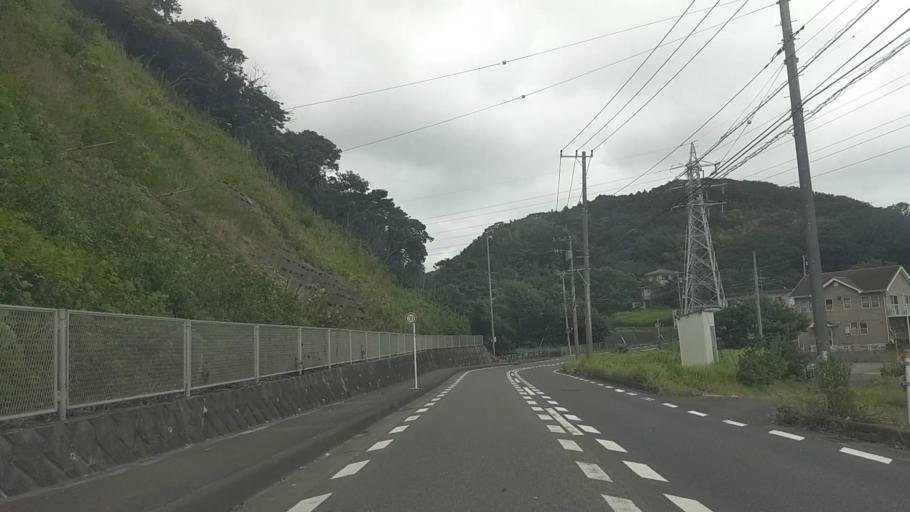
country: JP
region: Kanagawa
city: Yokosuka
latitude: 35.2343
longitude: 139.6344
